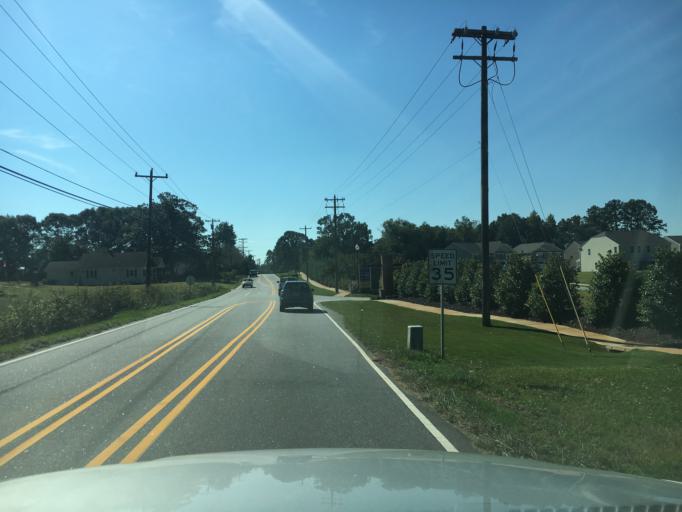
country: US
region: South Carolina
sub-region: Greenville County
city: Taylors
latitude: 34.9299
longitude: -82.2691
